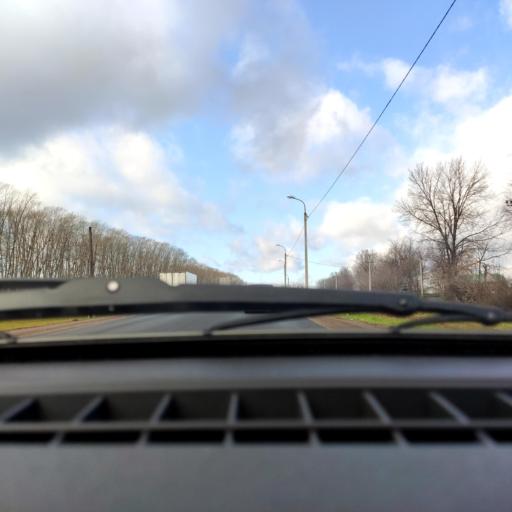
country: RU
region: Bashkortostan
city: Kabakovo
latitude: 54.6277
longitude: 56.1021
